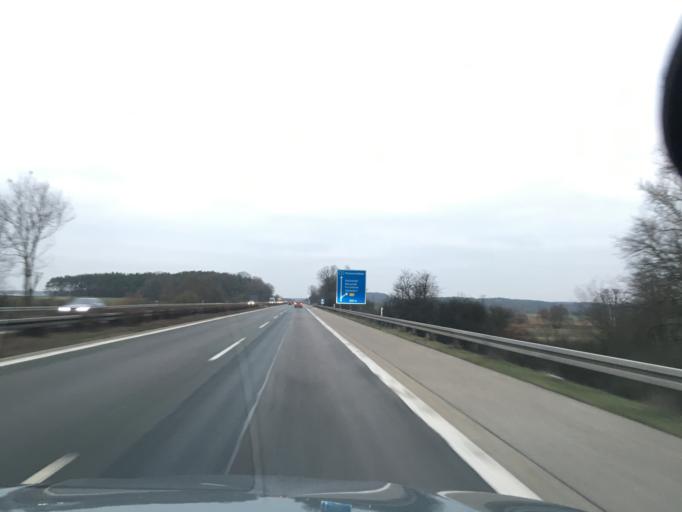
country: DE
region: Bavaria
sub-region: Regierungsbezirk Mittelfranken
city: Gremsdorf
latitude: 49.6920
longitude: 10.8592
